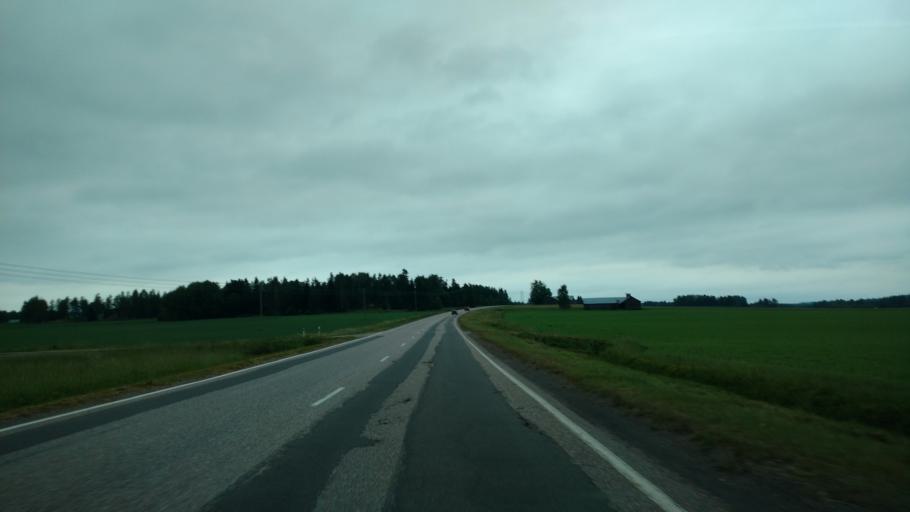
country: FI
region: Varsinais-Suomi
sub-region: Salo
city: Kiikala
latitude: 60.3970
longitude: 23.5843
